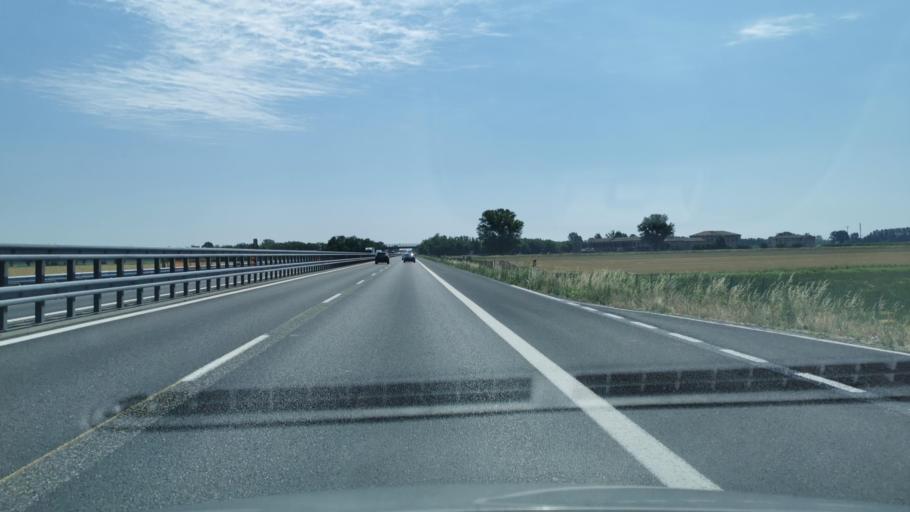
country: IT
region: Emilia-Romagna
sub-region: Provincia di Piacenza
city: Sarmato
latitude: 45.0711
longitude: 9.4878
